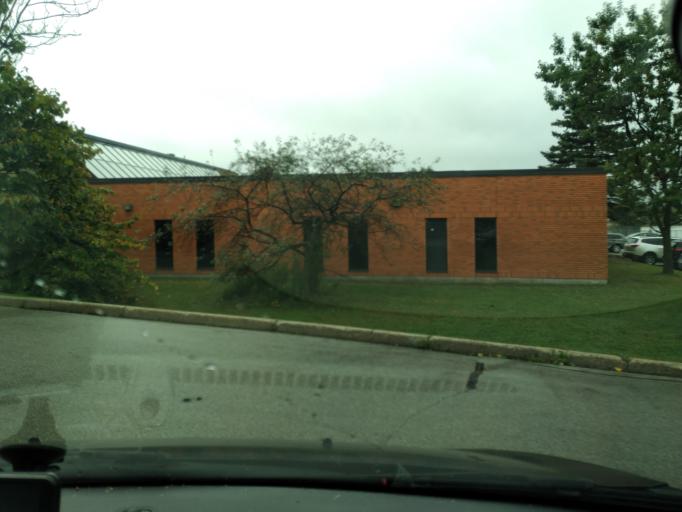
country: CA
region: Ontario
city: Barrie
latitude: 44.4110
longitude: -79.6805
